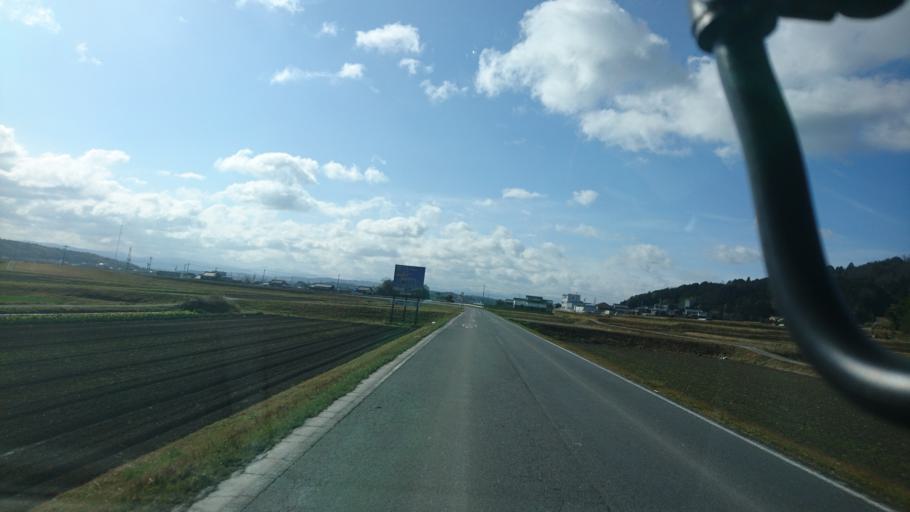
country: JP
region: Mie
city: Ueno-ebisumachi
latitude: 34.7617
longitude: 136.1094
